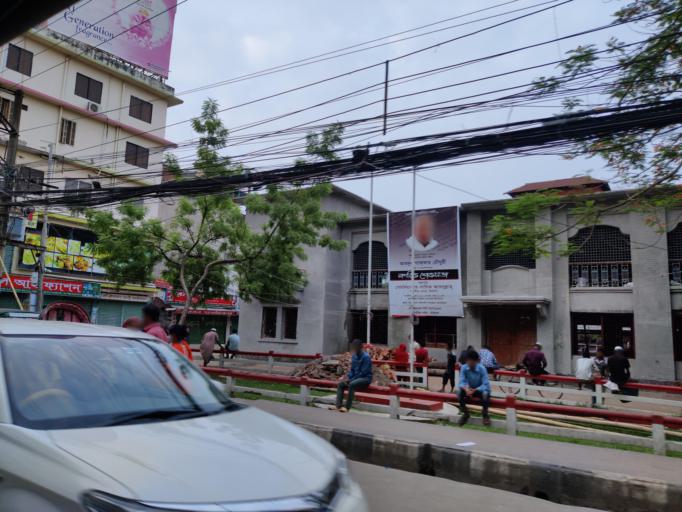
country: BD
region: Barisal
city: Barisal
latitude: 22.7047
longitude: 90.3707
